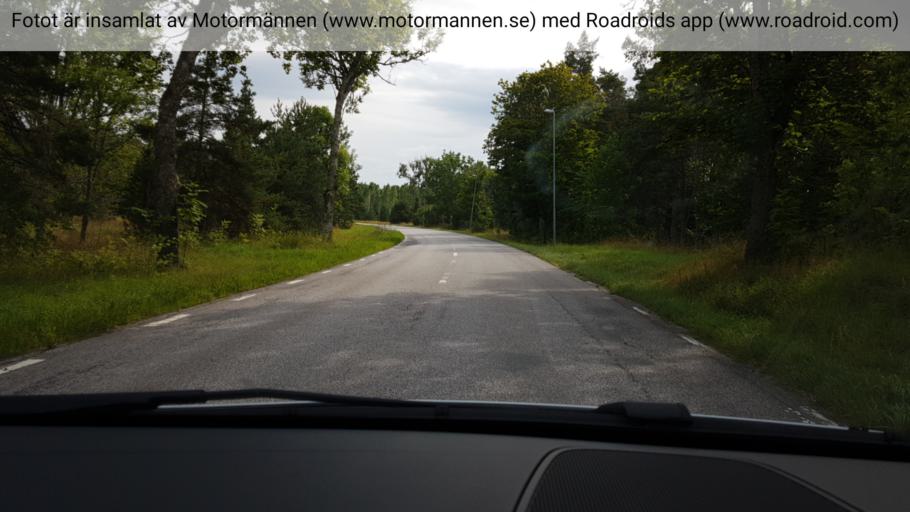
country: SE
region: Uppsala
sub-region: Osthammars Kommun
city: Anneberg
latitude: 60.1780
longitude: 18.3993
